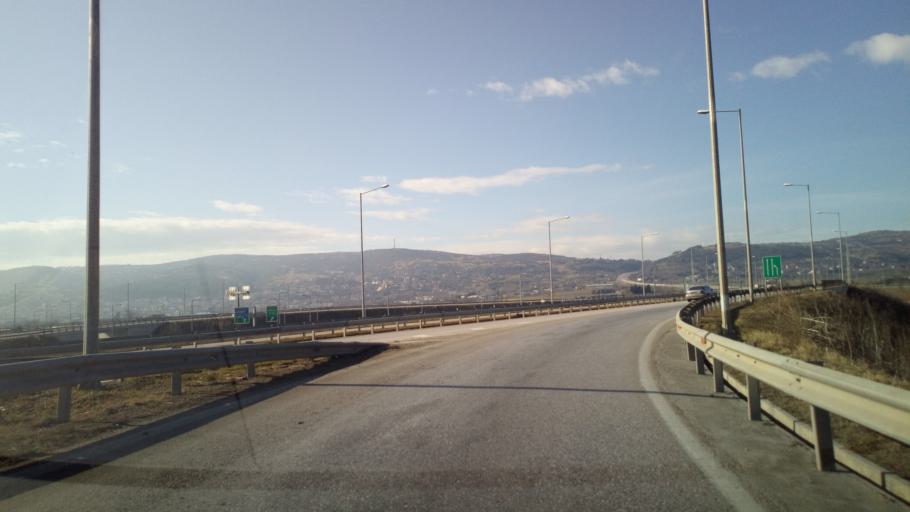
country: GR
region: Central Macedonia
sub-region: Nomos Thessalonikis
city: Lagyna
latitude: 40.7397
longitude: 23.0122
